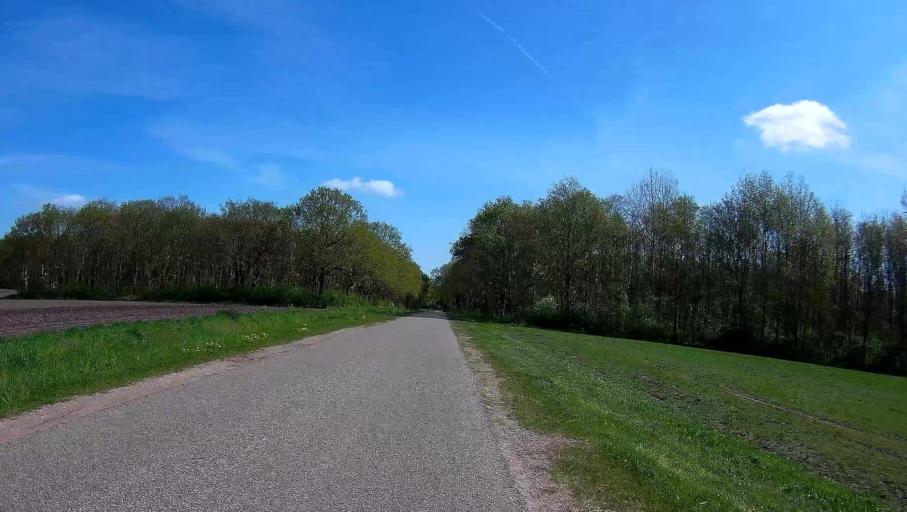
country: NL
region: Drenthe
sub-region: Gemeente Borger-Odoorn
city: Borger
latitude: 52.9936
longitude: 6.7824
